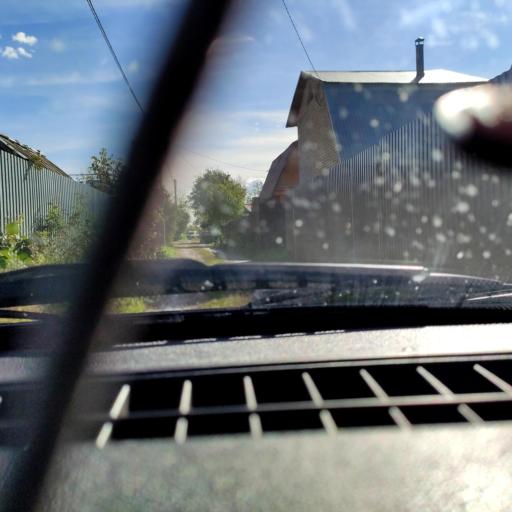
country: RU
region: Bashkortostan
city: Iglino
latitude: 54.7766
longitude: 56.2089
